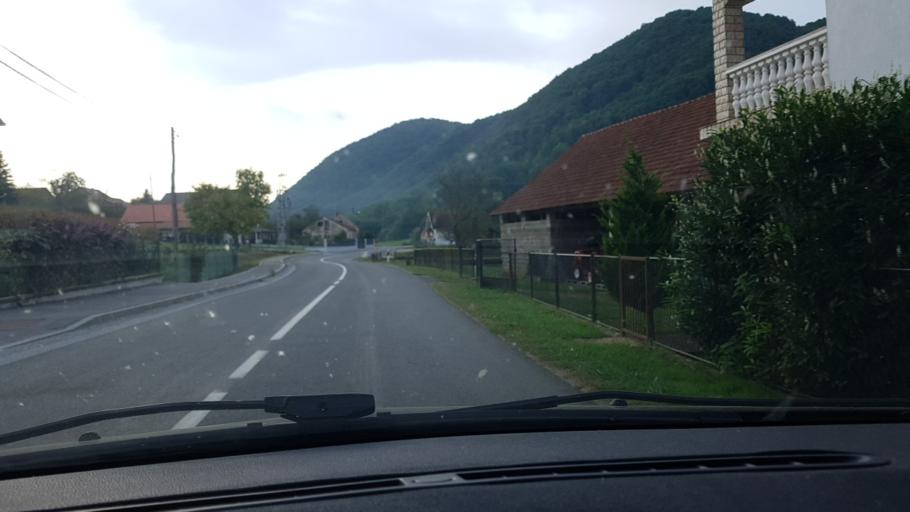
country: HR
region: Krapinsko-Zagorska
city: Mihovljan
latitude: 46.1226
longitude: 15.9898
